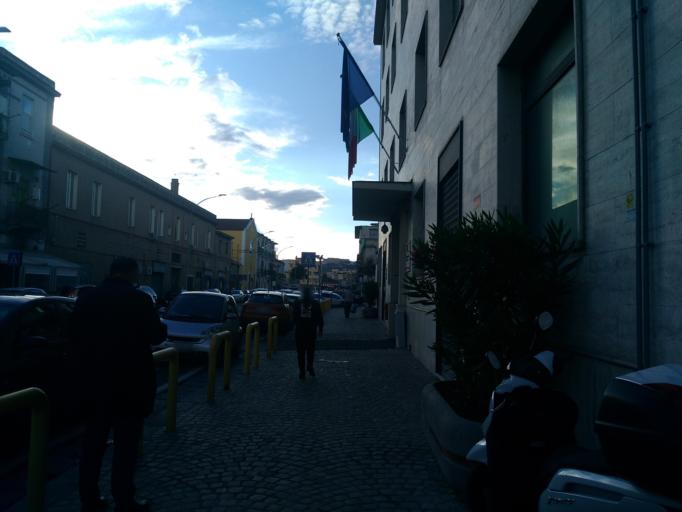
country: IT
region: Campania
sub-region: Provincia di Napoli
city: Napoli
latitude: 40.8500
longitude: 14.2877
